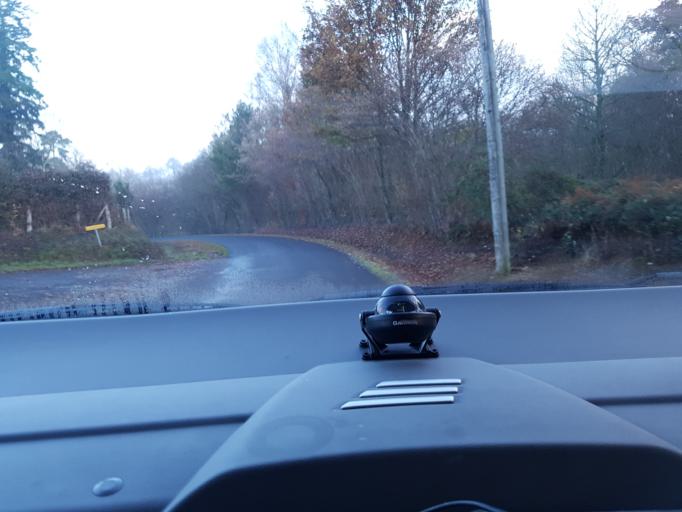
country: FR
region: Lower Normandy
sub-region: Departement de l'Orne
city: Champsecret
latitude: 48.6355
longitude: -0.5804
